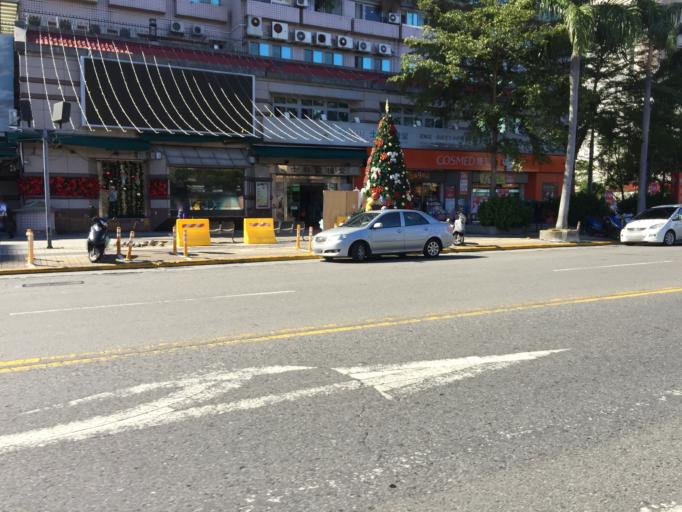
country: TW
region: Taipei
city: Taipei
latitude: 25.0885
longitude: 121.5236
